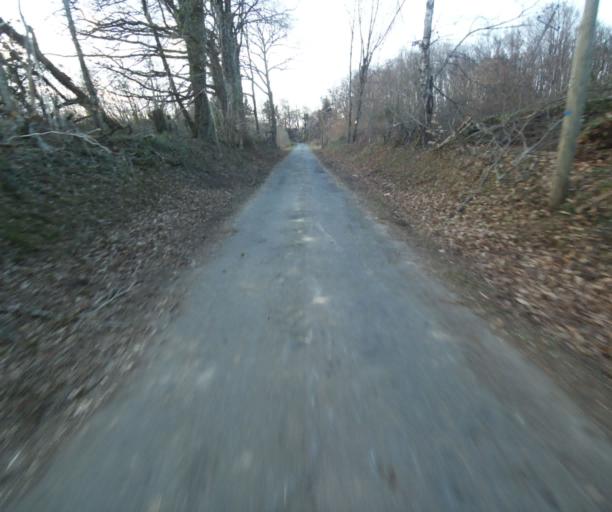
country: FR
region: Limousin
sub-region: Departement de la Correze
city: Uzerche
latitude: 45.3683
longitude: 1.5873
